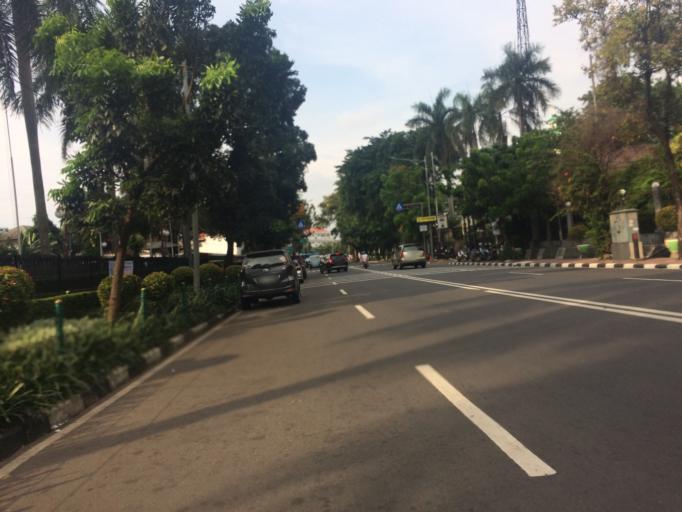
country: ID
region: Jakarta Raya
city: Jakarta
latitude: -6.1704
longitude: 106.8384
